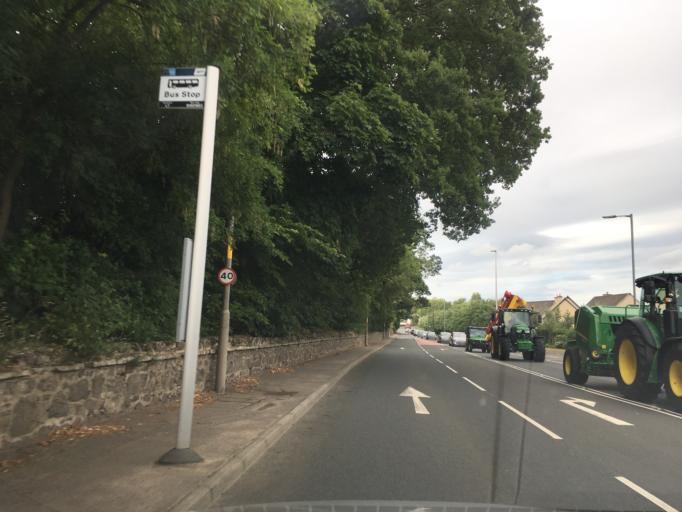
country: GB
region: Scotland
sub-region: South Lanarkshire
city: Biggar
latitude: 55.6168
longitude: -3.5371
